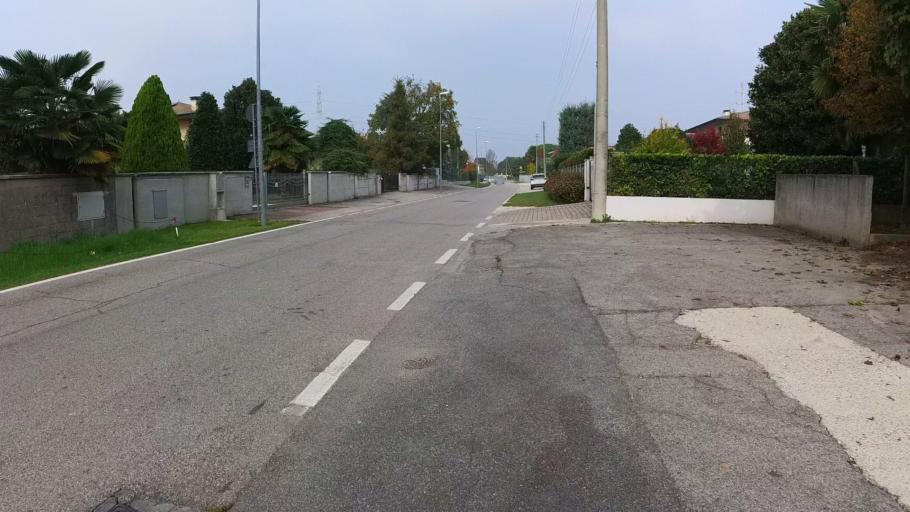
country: IT
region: Veneto
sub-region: Provincia di Venezia
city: Fosso
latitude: 45.3881
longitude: 12.0417
